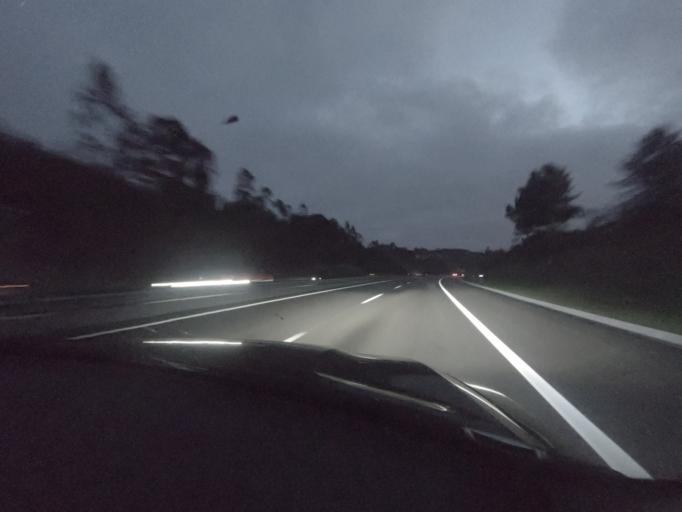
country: PT
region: Leiria
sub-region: Leiria
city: Caranguejeira
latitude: 39.7831
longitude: -8.7373
